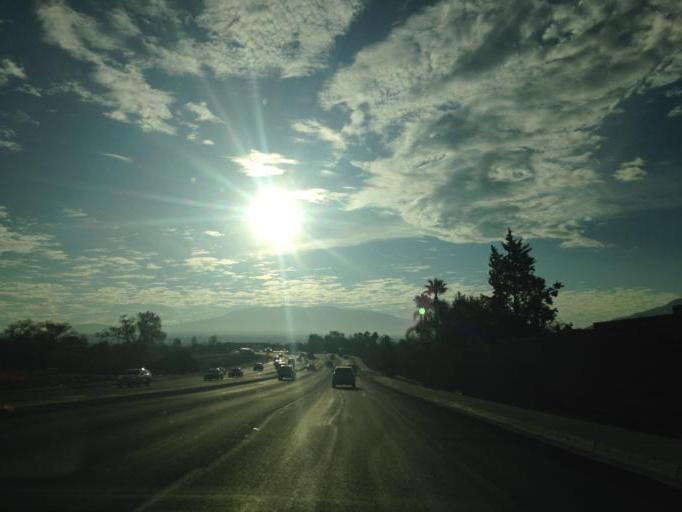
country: US
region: California
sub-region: Riverside County
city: Temecula
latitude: 33.4774
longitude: -117.1342
